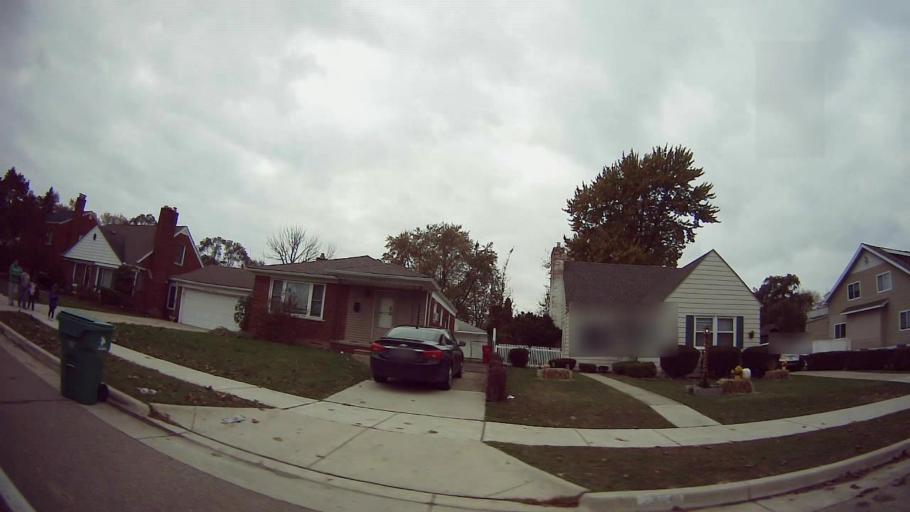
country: US
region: Michigan
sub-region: Macomb County
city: Eastpointe
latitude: 42.4694
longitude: -82.9668
